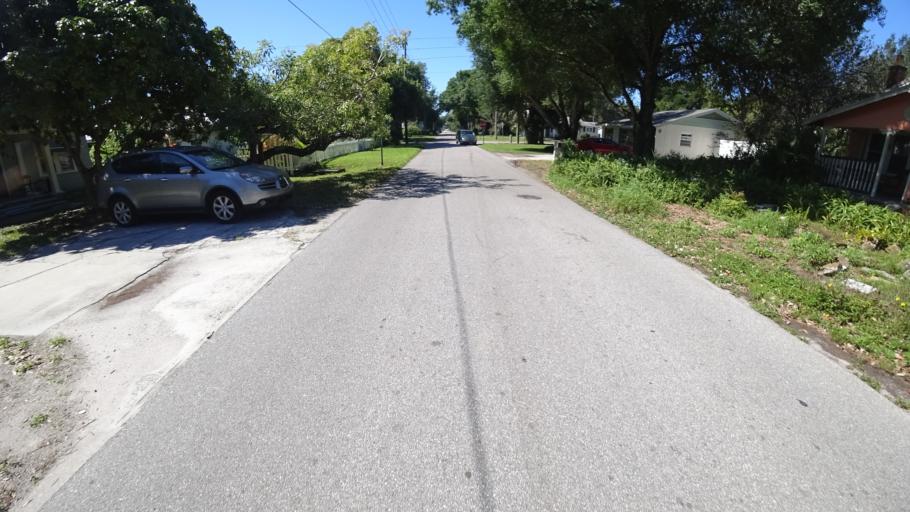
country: US
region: Florida
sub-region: Manatee County
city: West Bradenton
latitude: 27.4942
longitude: -82.5961
